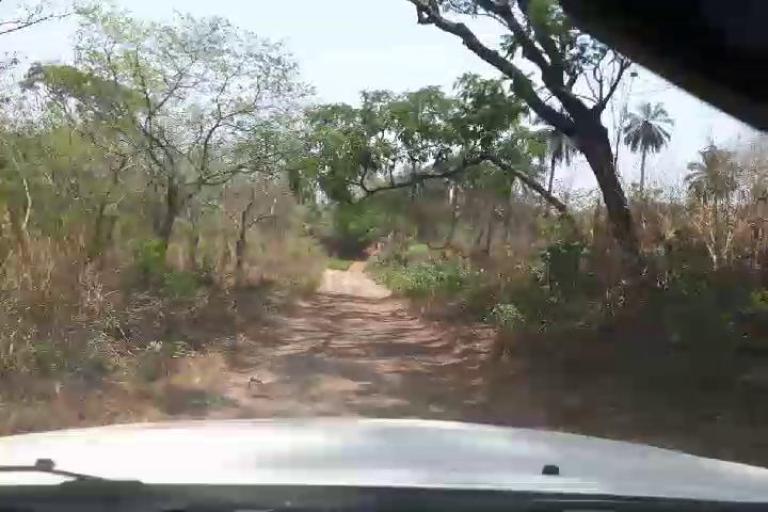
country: SL
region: Northern Province
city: Alikalia
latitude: 9.0745
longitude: -11.4772
